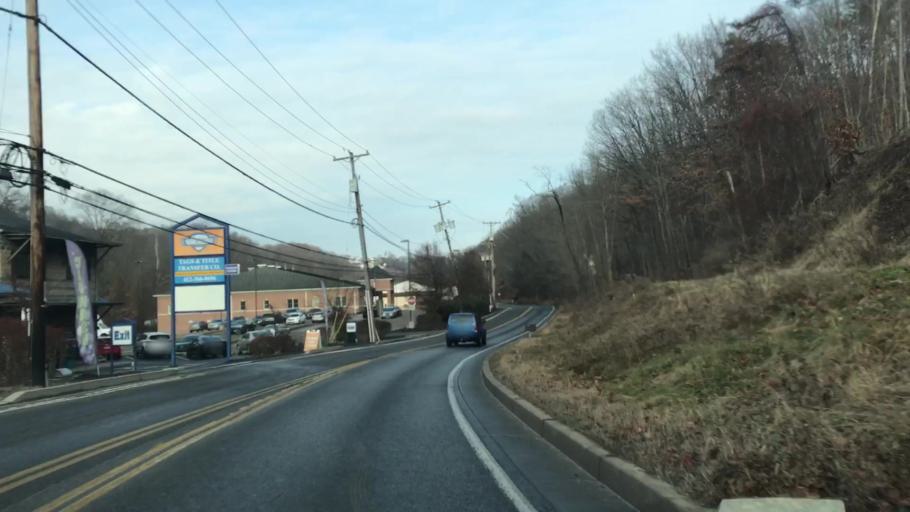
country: US
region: Pennsylvania
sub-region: Allegheny County
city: Ben Avon
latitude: 40.5349
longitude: -80.0725
